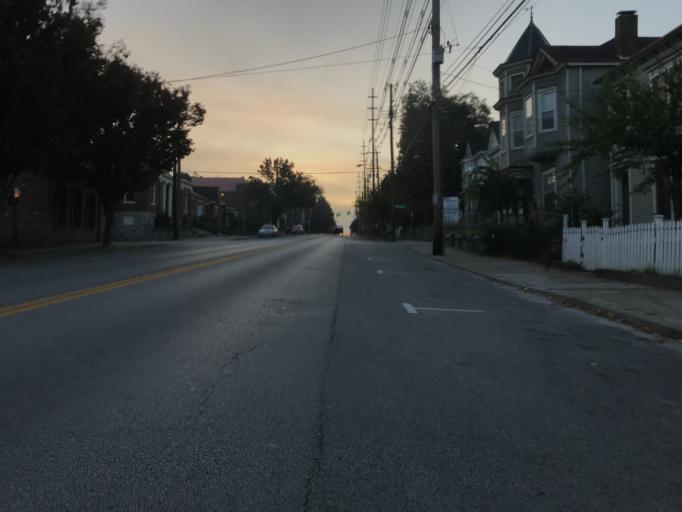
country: US
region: Indiana
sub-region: Clark County
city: Jeffersonville
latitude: 38.2573
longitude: -85.7183
